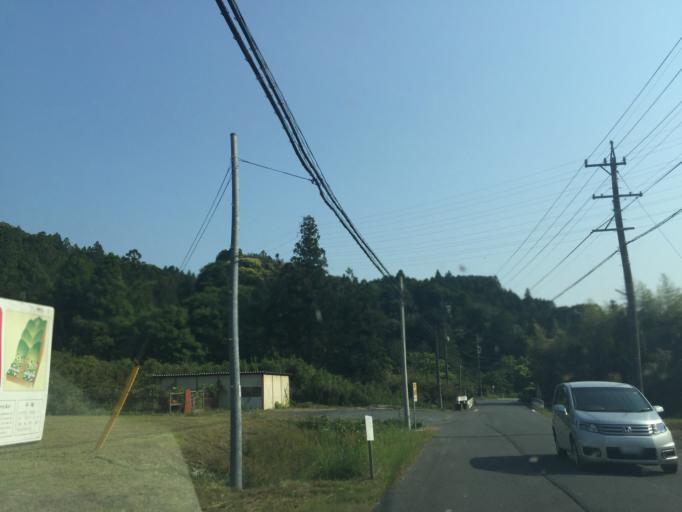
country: JP
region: Shizuoka
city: Kakegawa
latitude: 34.8259
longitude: 138.0434
